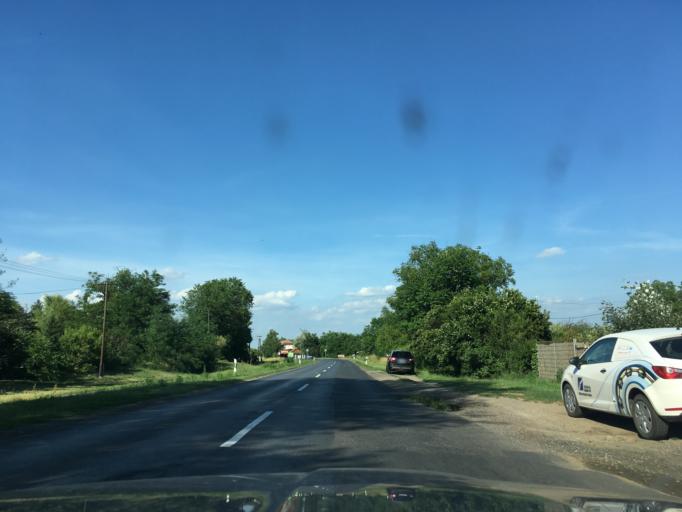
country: HU
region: Hajdu-Bihar
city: Hajdusamson
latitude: 47.5784
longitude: 21.7102
